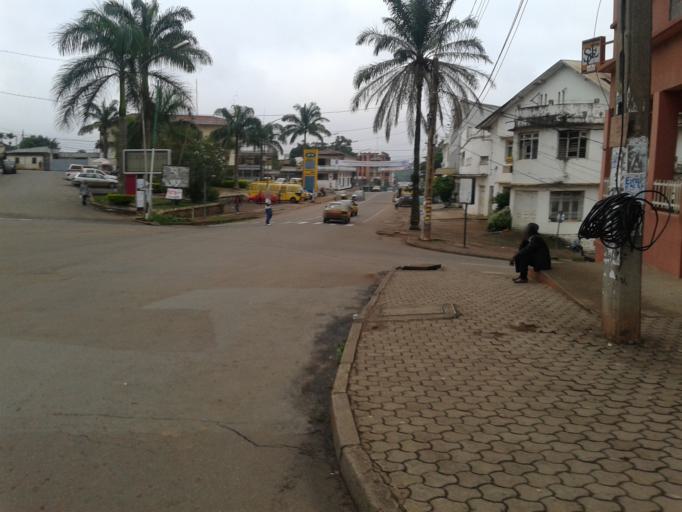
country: CM
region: Centre
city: Yaounde
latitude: 3.8711
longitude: 11.5172
